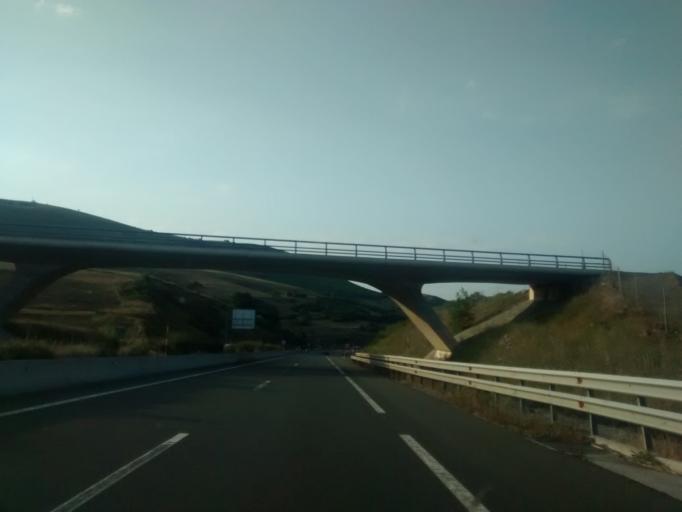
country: ES
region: Cantabria
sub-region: Provincia de Cantabria
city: Pesquera
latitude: 43.0762
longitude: -4.0858
